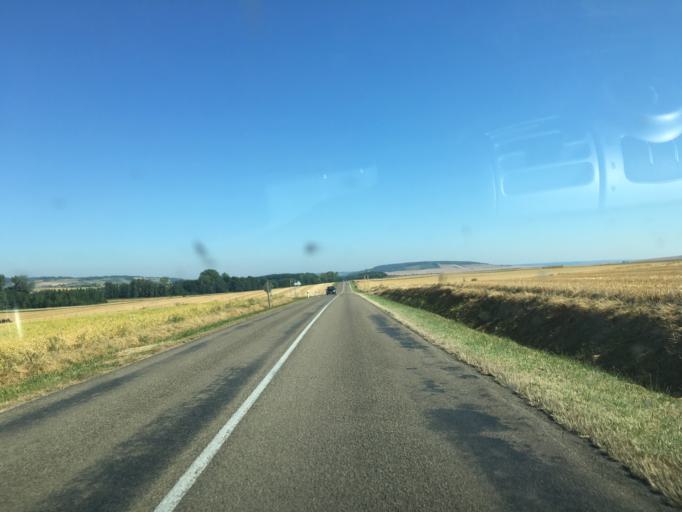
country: FR
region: Bourgogne
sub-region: Departement de l'Yonne
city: Aillant-sur-Tholon
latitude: 47.8835
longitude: 3.3522
